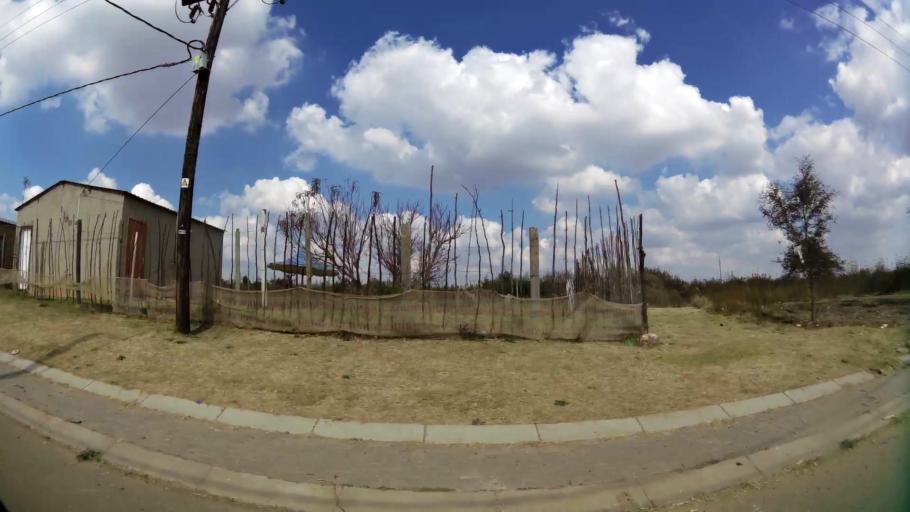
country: ZA
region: Gauteng
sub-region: City of Johannesburg Metropolitan Municipality
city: Roodepoort
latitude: -26.1851
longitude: 27.8454
